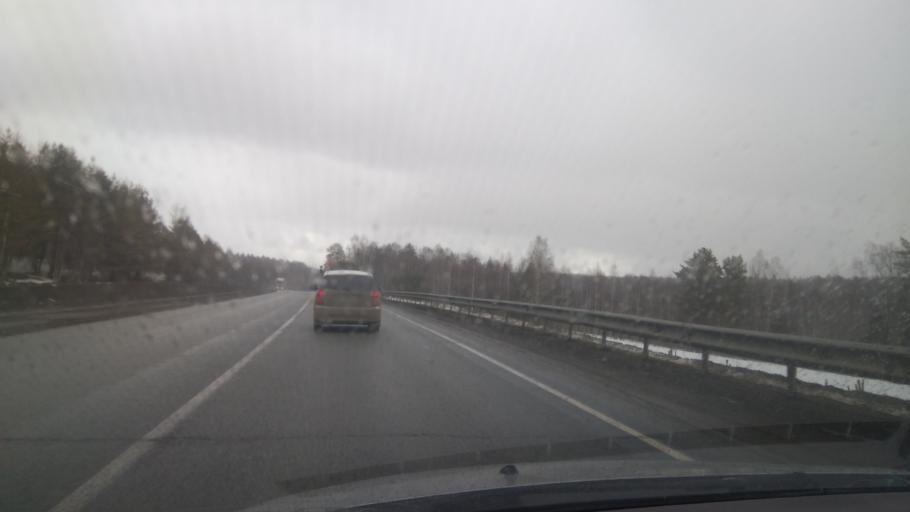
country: RU
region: Sverdlovsk
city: Ufimskiy
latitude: 56.7784
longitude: 58.2575
